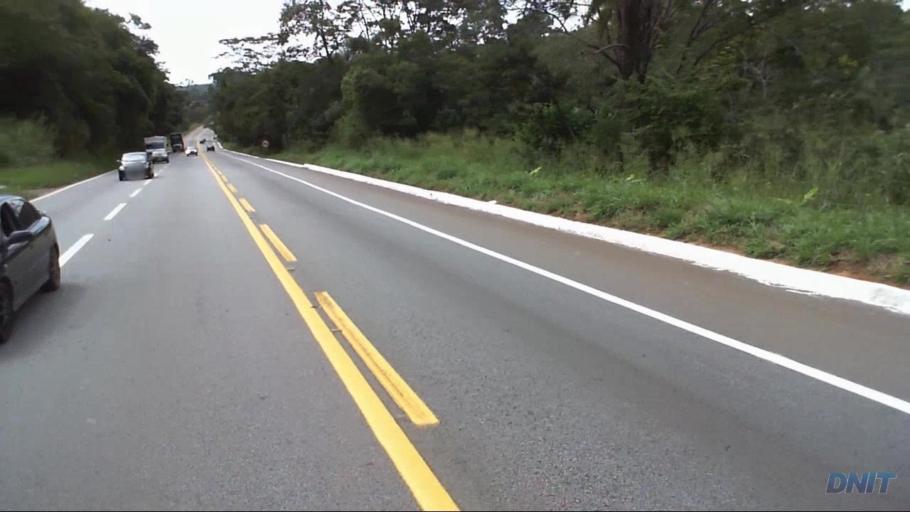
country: BR
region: Minas Gerais
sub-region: Santa Luzia
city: Santa Luzia
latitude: -19.7974
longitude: -43.7483
